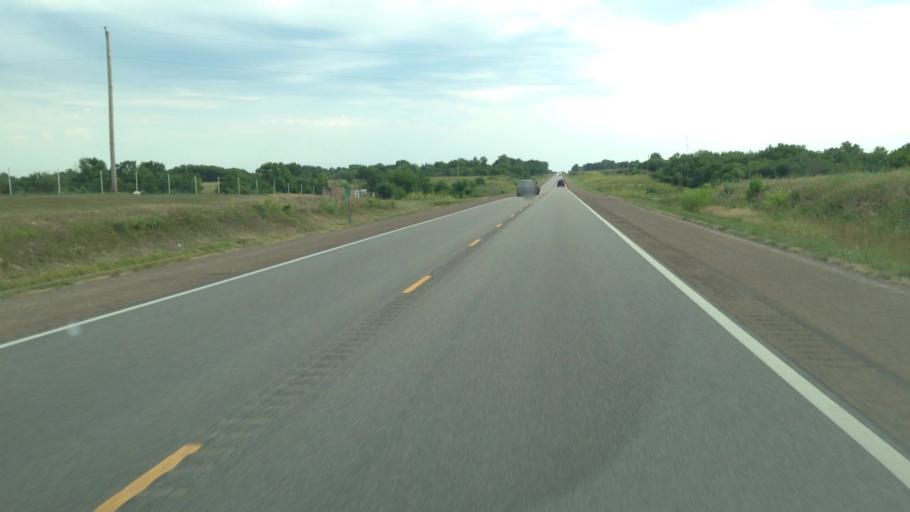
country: US
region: Kansas
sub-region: Woodson County
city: Yates Center
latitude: 38.0003
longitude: -95.7389
